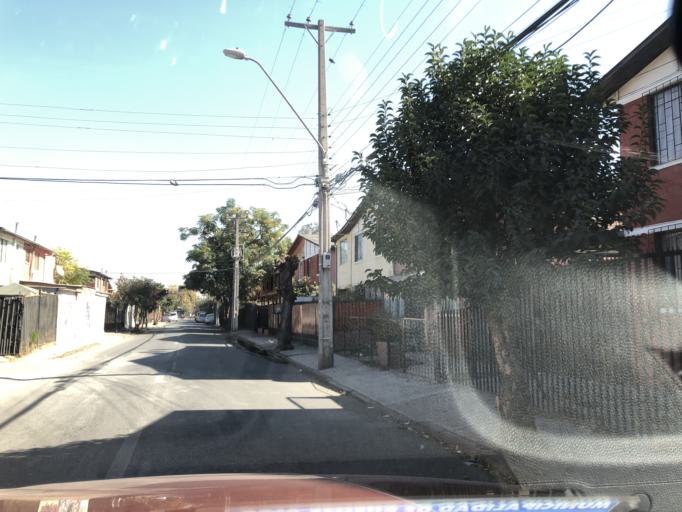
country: CL
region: Santiago Metropolitan
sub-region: Provincia de Cordillera
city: Puente Alto
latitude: -33.5644
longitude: -70.5778
